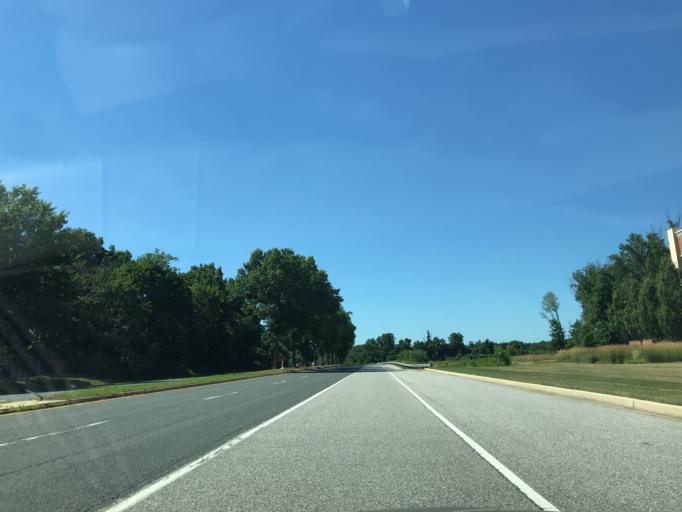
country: US
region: Maryland
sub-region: Harford County
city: Aberdeen
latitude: 39.5021
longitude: -76.1502
